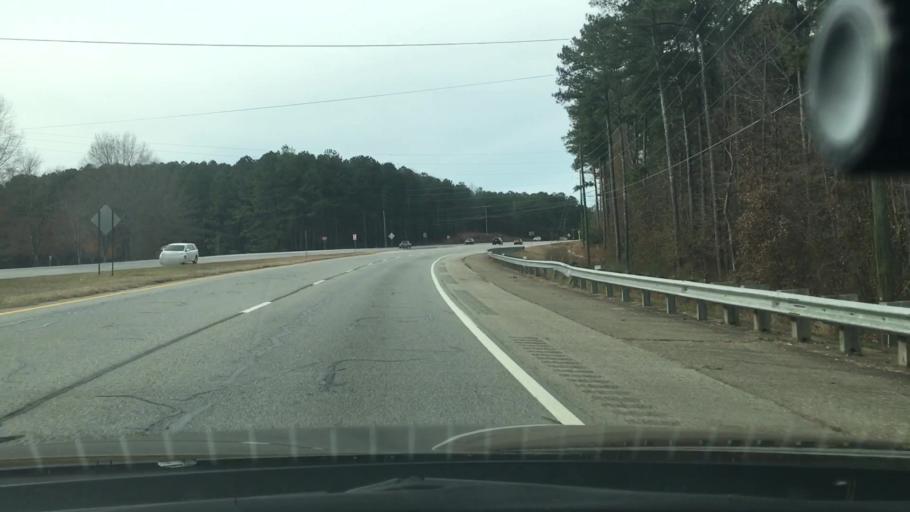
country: US
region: Georgia
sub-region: Fayette County
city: Peachtree City
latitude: 33.3995
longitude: -84.6583
